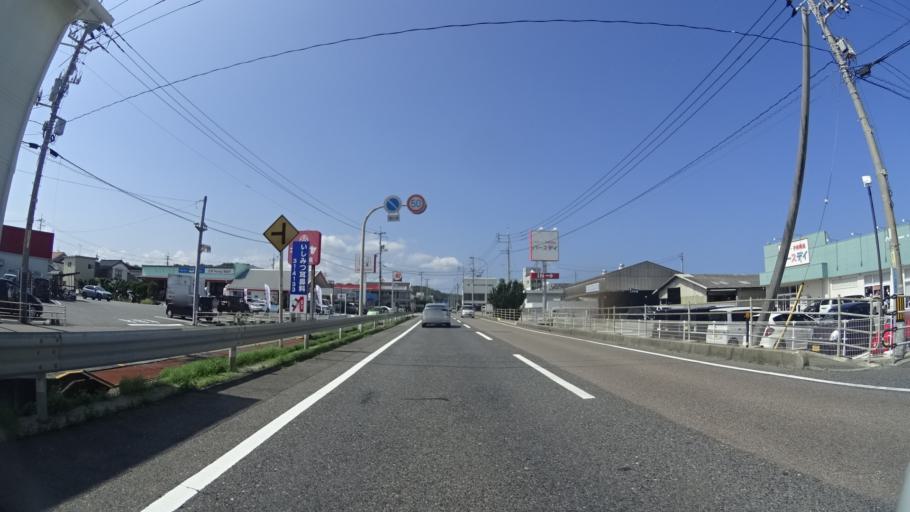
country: JP
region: Shimane
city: Masuda
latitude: 34.6900
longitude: 131.8090
